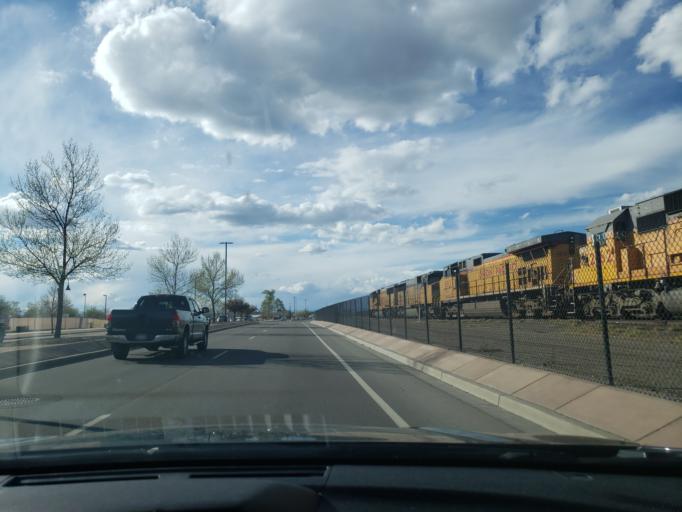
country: US
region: Colorado
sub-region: Mesa County
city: Grand Junction
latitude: 39.0717
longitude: -108.5801
